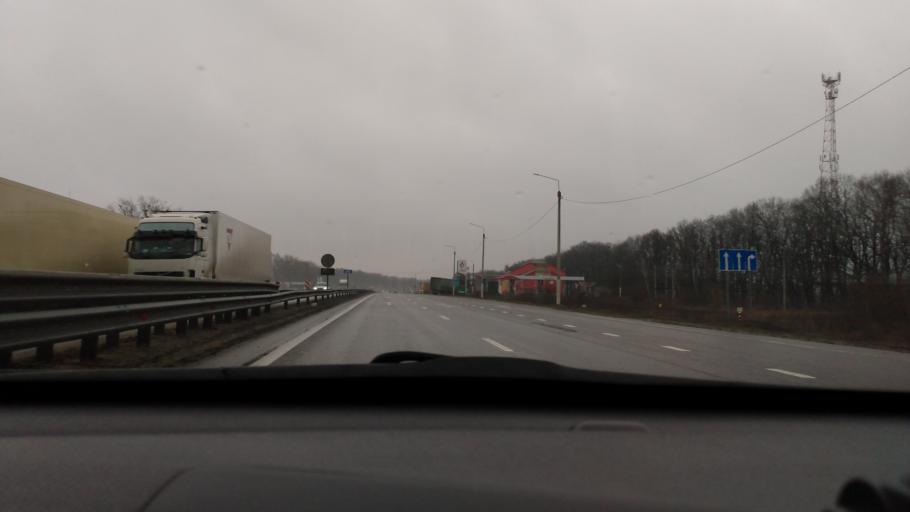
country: RU
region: Tula
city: Shvartsevskiy
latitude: 54.1082
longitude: 38.0568
